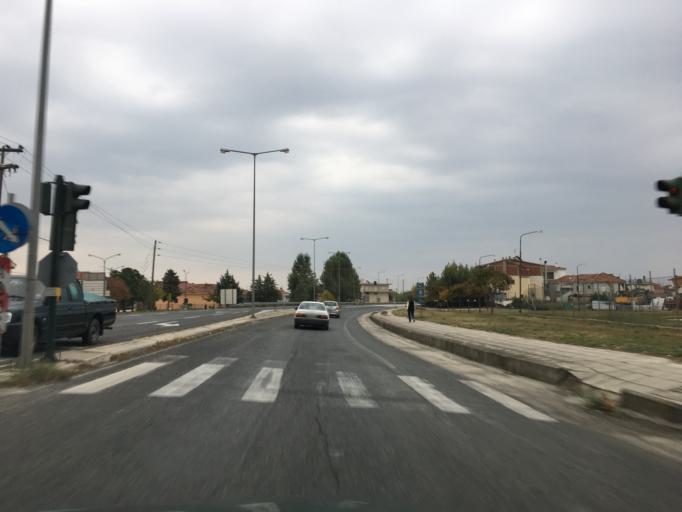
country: GR
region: Thessaly
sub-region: Trikala
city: Trikala
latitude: 39.5657
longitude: 21.7775
